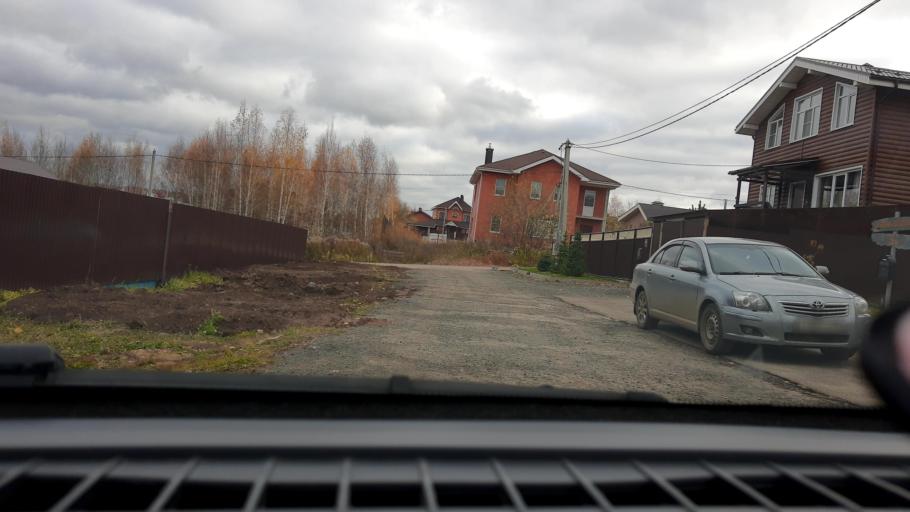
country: RU
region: Nizjnij Novgorod
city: Afonino
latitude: 56.2651
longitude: 44.0690
